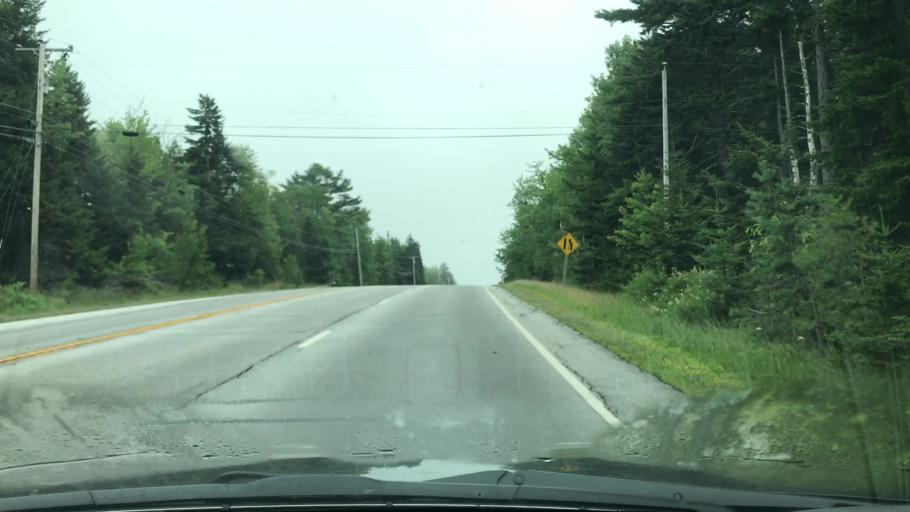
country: US
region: Maine
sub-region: Waldo County
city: Northport
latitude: 44.3089
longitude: -68.9742
